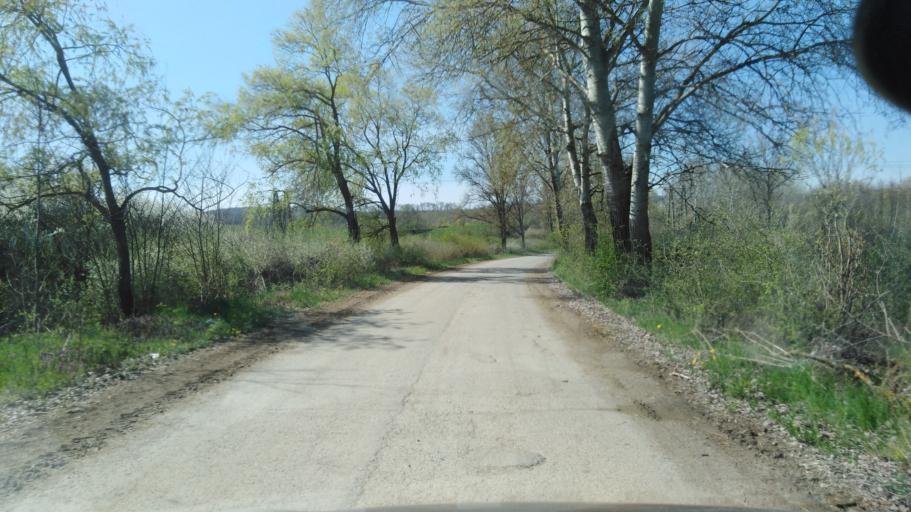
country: HU
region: Nograd
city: Karancskeszi
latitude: 48.1987
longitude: 19.6193
